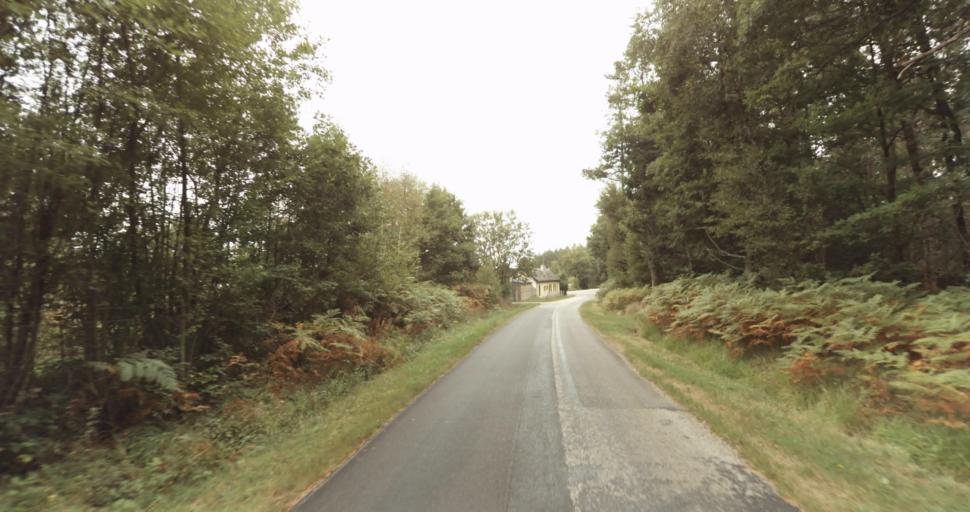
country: FR
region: Lower Normandy
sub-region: Departement de l'Orne
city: Gace
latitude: 48.8306
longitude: 0.3370
